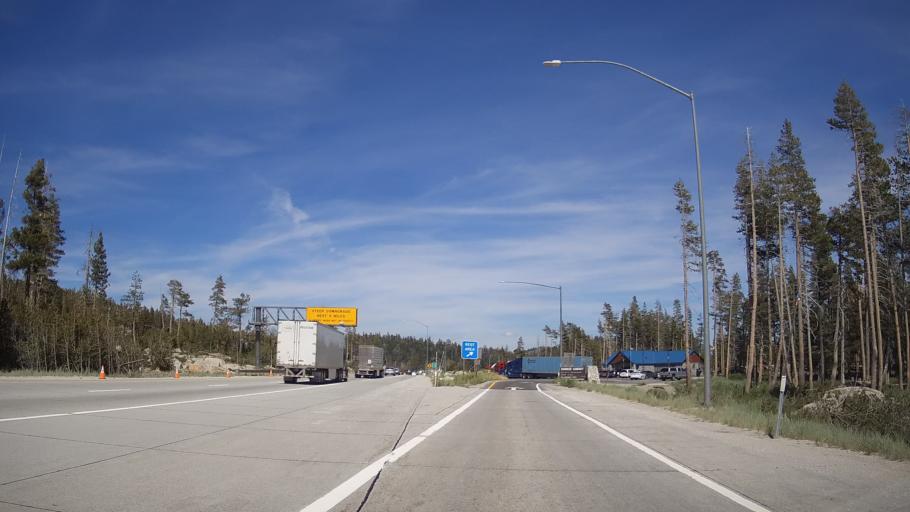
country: US
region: California
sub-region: Nevada County
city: Truckee
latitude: 39.3407
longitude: -120.3423
